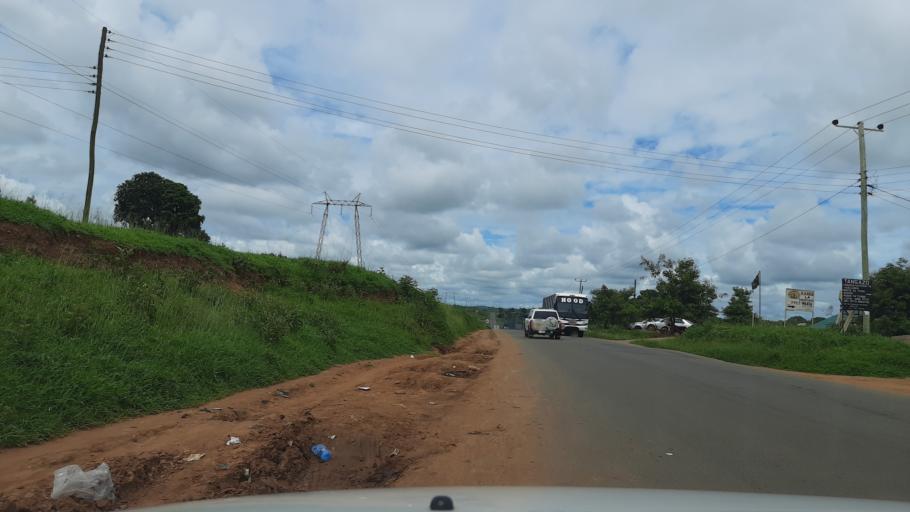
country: TZ
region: Tanga
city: Chanika
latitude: -5.7826
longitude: 38.2932
